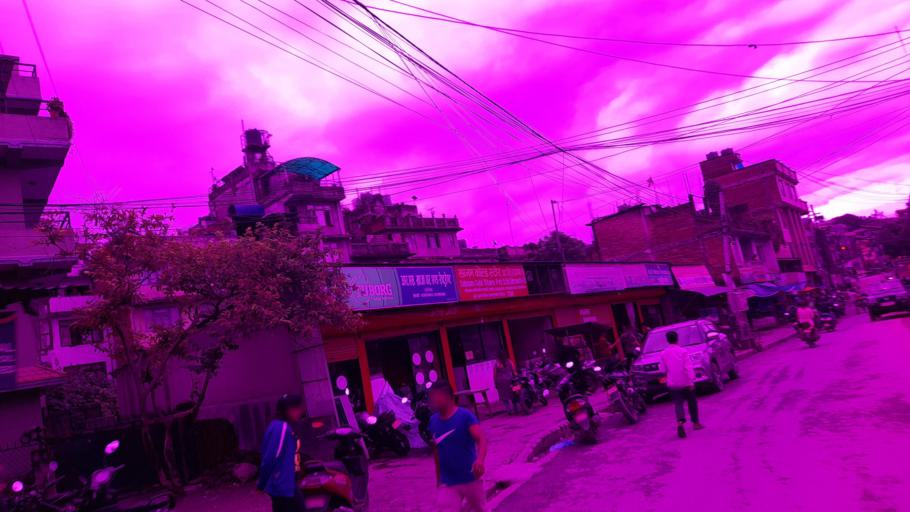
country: NP
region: Central Region
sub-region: Bagmati Zone
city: Kathmandu
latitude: 27.7029
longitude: 85.3023
